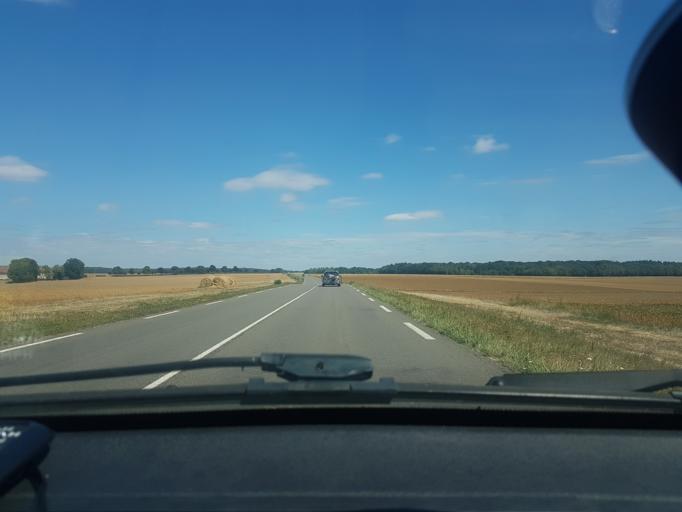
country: FR
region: Bourgogne
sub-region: Departement de la Cote-d'Or
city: Arc-sur-Tille
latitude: 47.3528
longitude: 5.2060
